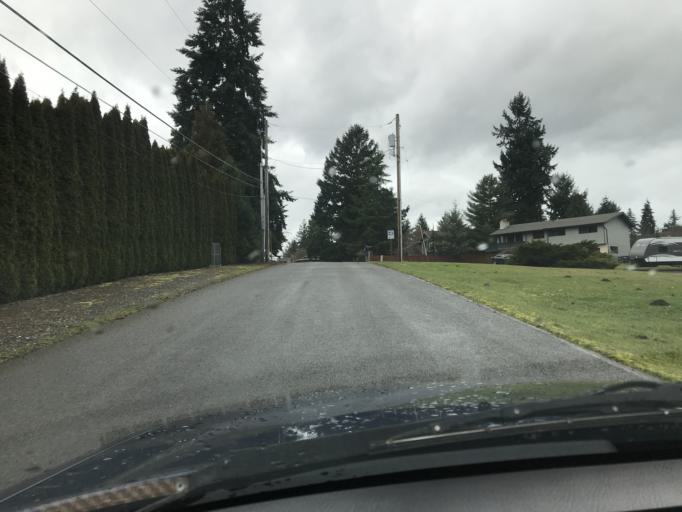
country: US
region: Washington
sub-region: Pierce County
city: Waller
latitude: 47.1883
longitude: -122.3726
